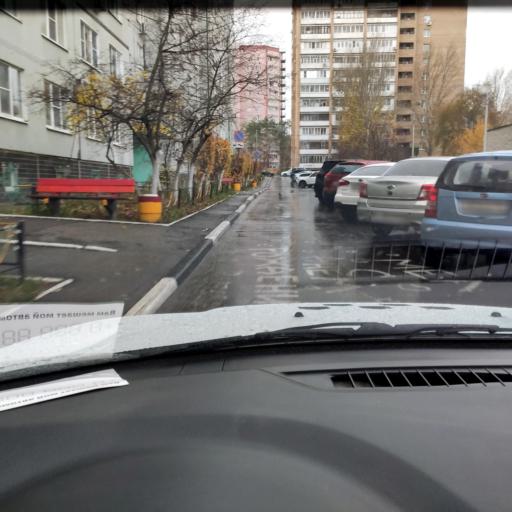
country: RU
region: Samara
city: Zhigulevsk
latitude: 53.4768
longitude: 49.4565
